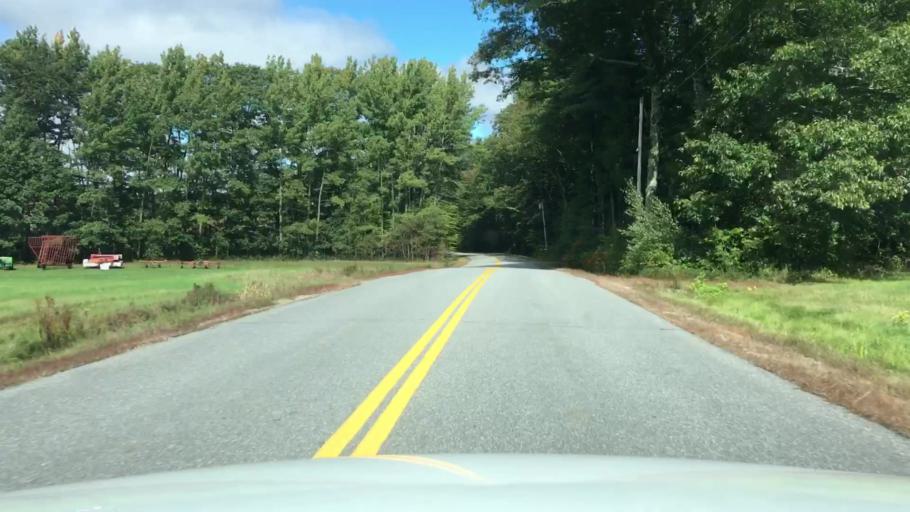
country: US
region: Maine
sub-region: Sagadahoc County
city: North Bath
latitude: 43.9522
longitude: -69.8941
